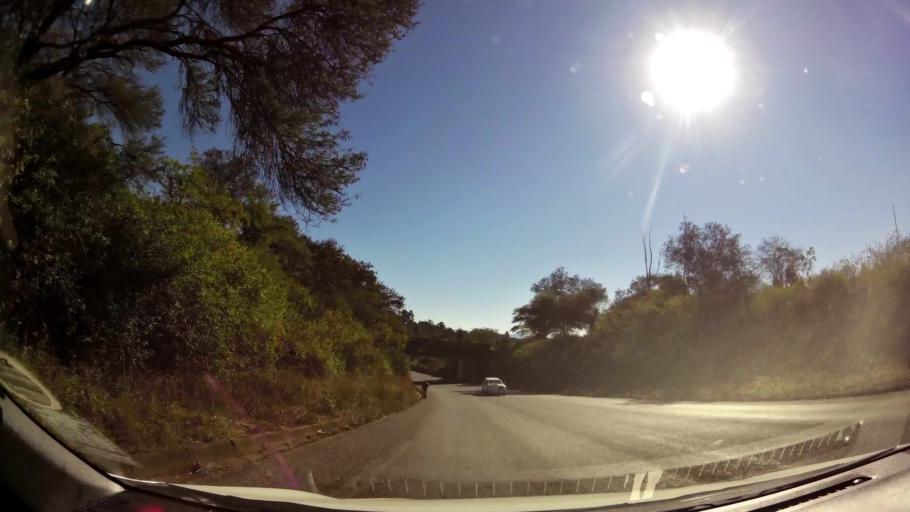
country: ZA
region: Limpopo
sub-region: Mopani District Municipality
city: Tzaneen
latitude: -23.8512
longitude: 30.1691
